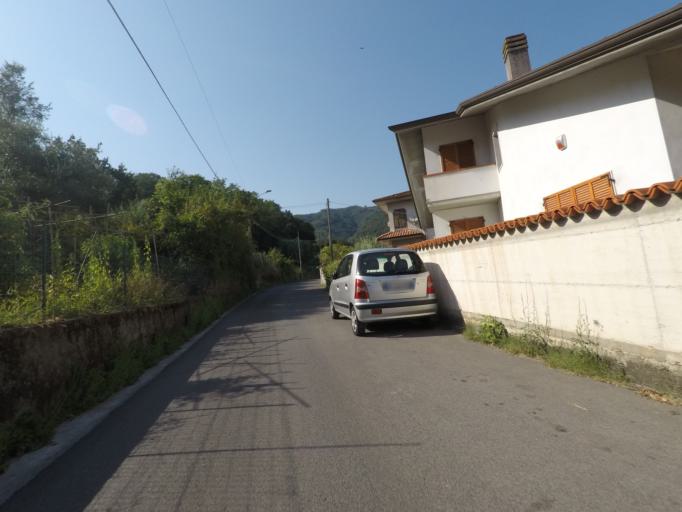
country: IT
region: Tuscany
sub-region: Provincia di Massa-Carrara
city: Carrara
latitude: 44.0745
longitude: 10.0750
